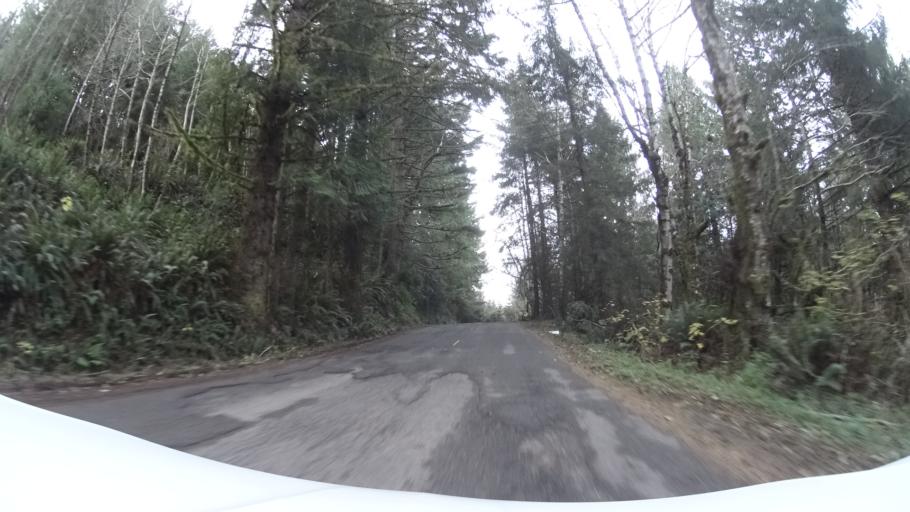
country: US
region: California
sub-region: Humboldt County
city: Ferndale
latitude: 40.5395
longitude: -124.2776
